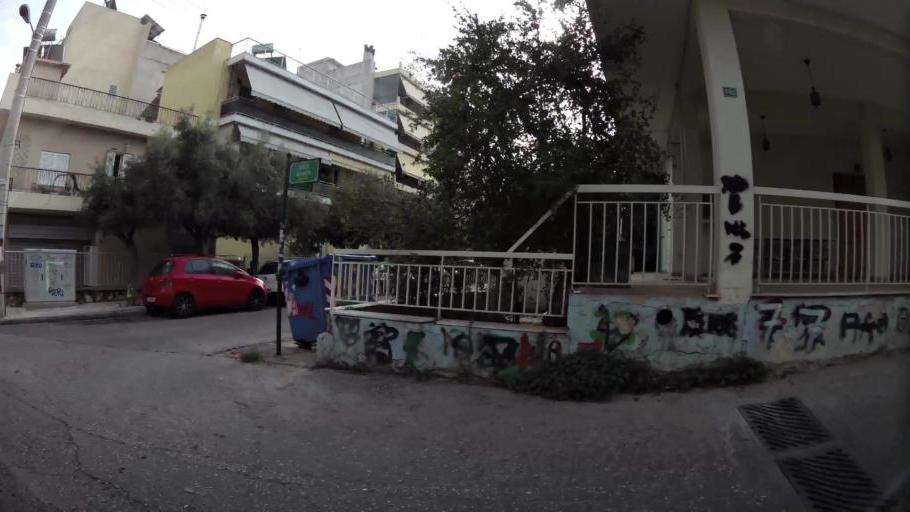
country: GR
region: Attica
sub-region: Nomarchia Athinas
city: Petroupolis
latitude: 38.0428
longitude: 23.6944
